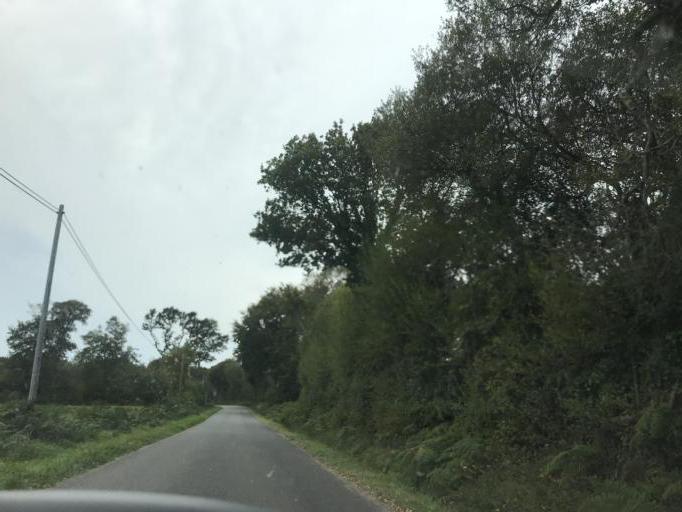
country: FR
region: Brittany
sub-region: Departement du Finistere
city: Plouneour-Menez
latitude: 48.3616
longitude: -3.8707
